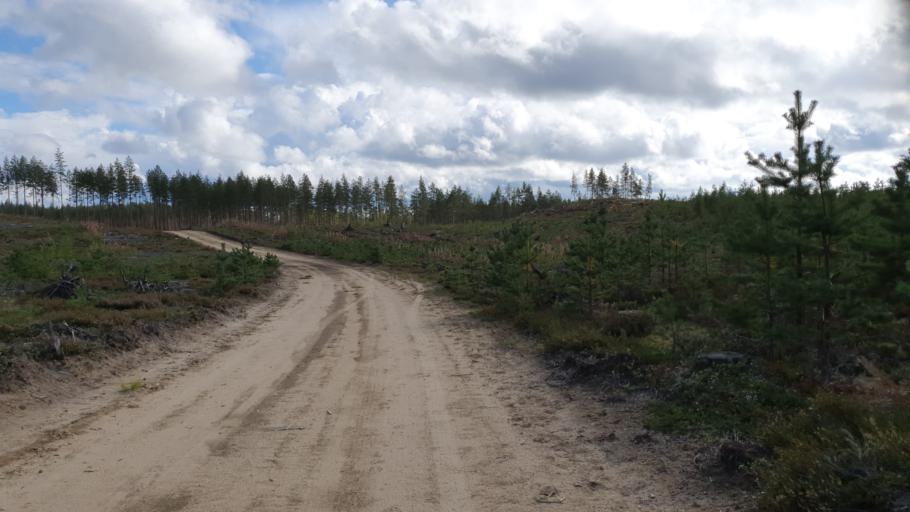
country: FI
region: Kainuu
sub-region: Kehys-Kainuu
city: Kuhmo
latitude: 64.1493
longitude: 29.3702
